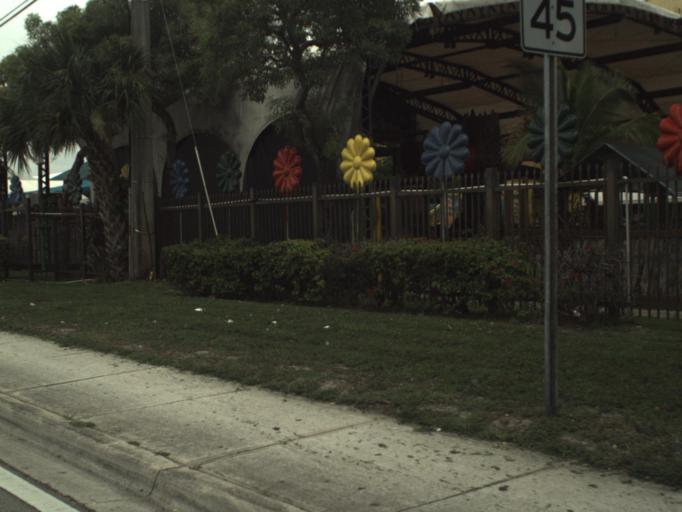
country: US
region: Florida
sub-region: Broward County
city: Washington Park
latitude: 26.1363
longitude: -80.1908
